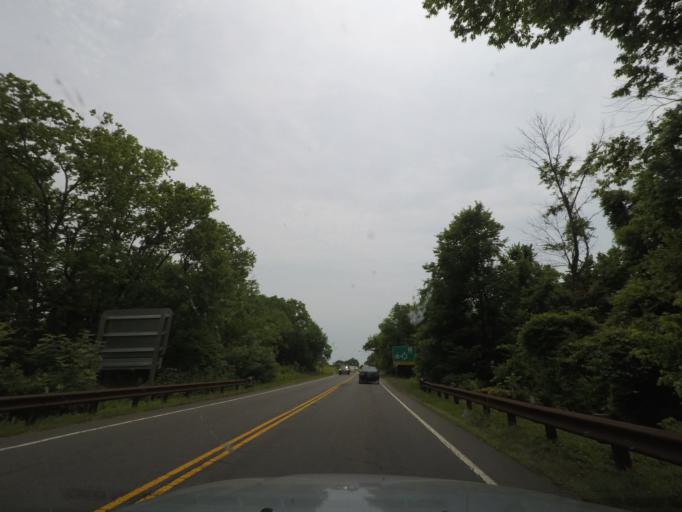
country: US
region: Virginia
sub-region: Prince William County
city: Bull Run Mountain Estates
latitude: 38.9671
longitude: -77.6226
